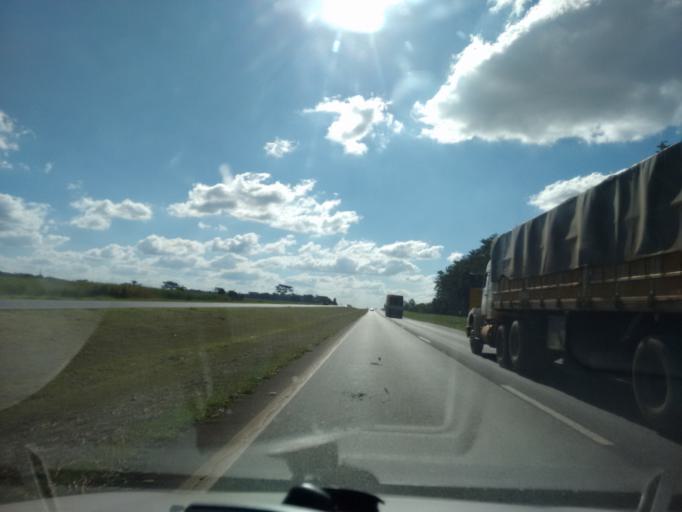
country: BR
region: Sao Paulo
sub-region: Araraquara
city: Araraquara
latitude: -21.8283
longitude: -48.1647
